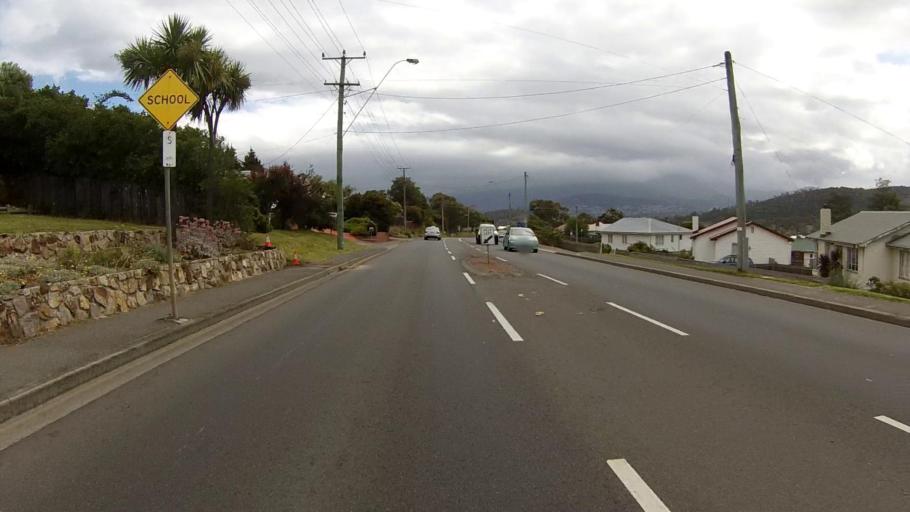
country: AU
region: Tasmania
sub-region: Clarence
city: Warrane
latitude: -42.8591
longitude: 147.3840
